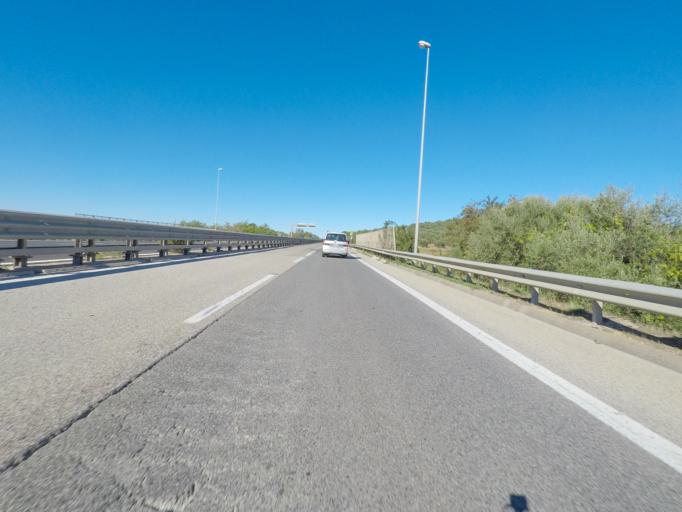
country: IT
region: Tuscany
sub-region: Provincia di Grosseto
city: Grosseto
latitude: 42.7330
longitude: 11.1362
